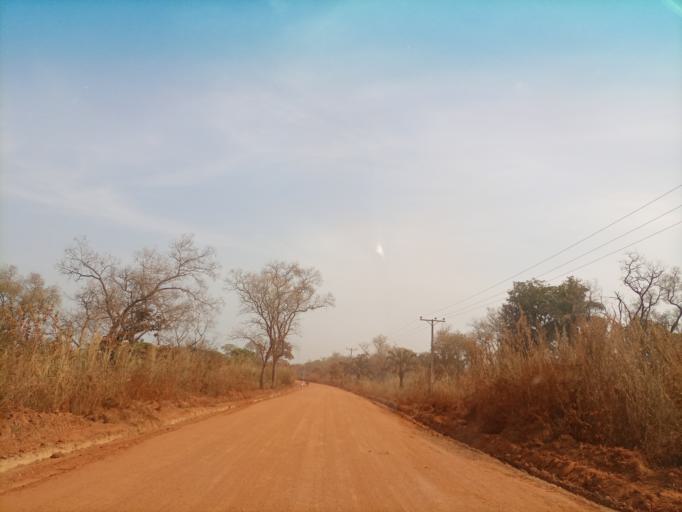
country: NG
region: Enugu
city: Eha Amufu
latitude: 6.6714
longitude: 7.7371
